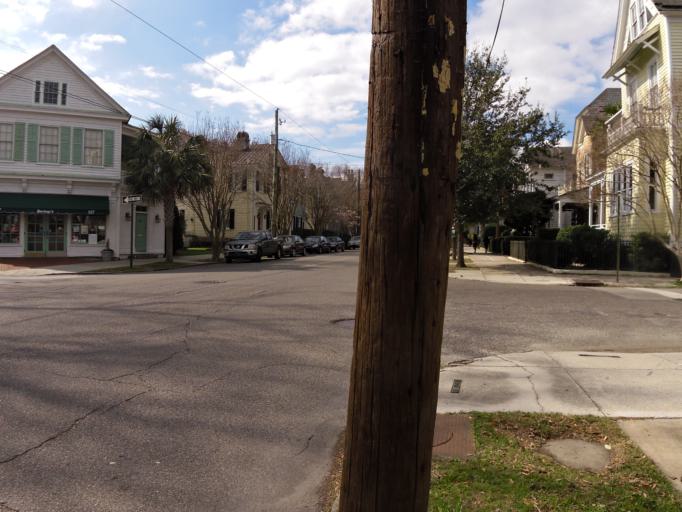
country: US
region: South Carolina
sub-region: Charleston County
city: Charleston
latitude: 32.7759
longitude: -79.9372
